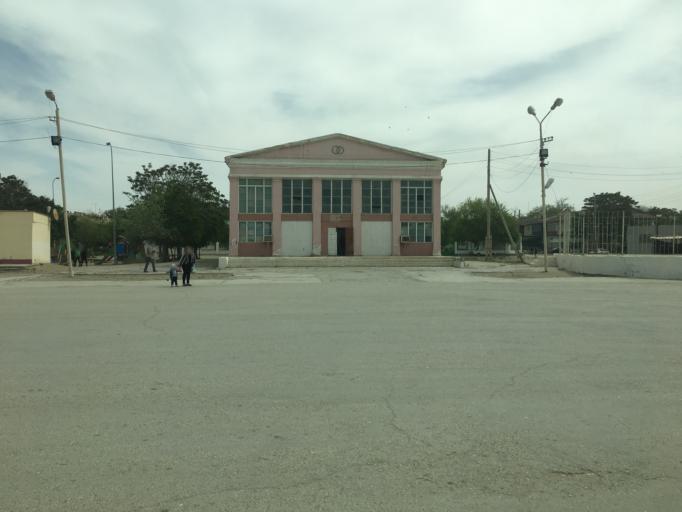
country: TM
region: Balkan
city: Turkmenbasy
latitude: 39.4037
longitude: 53.1263
